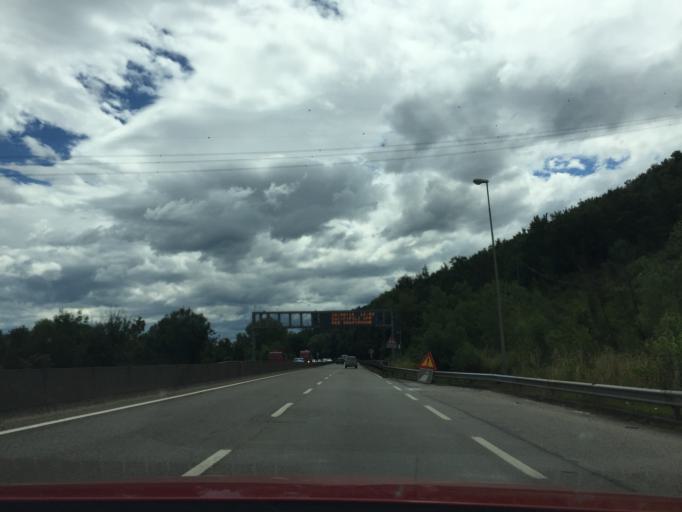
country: IT
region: Tuscany
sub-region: Province of Florence
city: Ginestra Fiorentina
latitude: 43.7137
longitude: 11.0435
